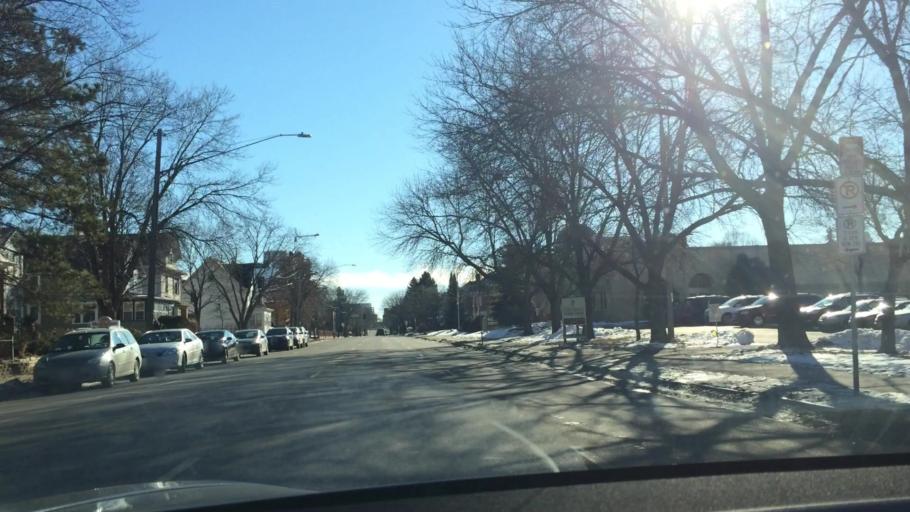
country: US
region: Minnesota
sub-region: Hennepin County
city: Minneapolis
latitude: 44.9955
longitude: -93.2616
